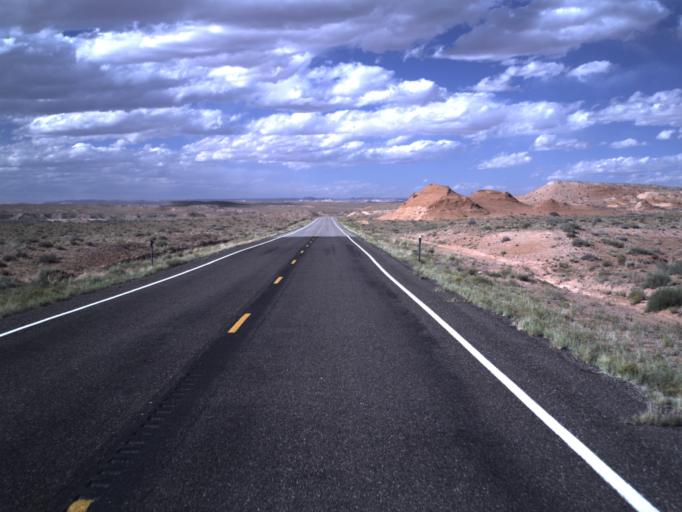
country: US
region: Utah
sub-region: Emery County
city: Ferron
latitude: 38.3088
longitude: -110.6716
